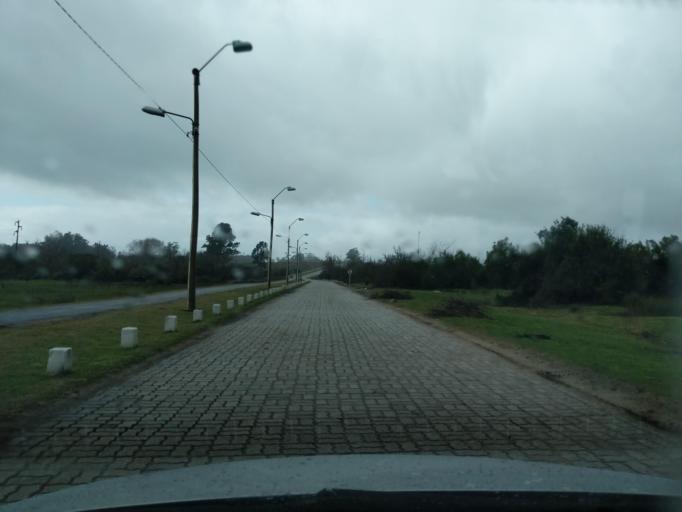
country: UY
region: Florida
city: Florida
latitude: -34.1090
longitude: -56.2034
